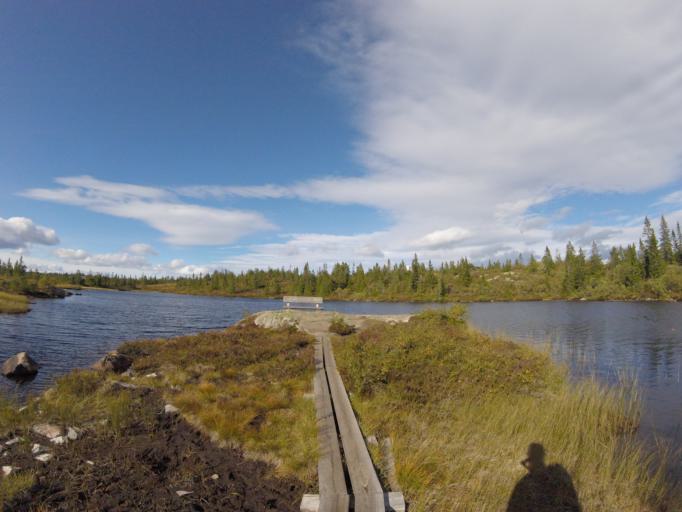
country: NO
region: Buskerud
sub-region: Flesberg
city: Lampeland
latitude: 59.7640
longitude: 9.4157
